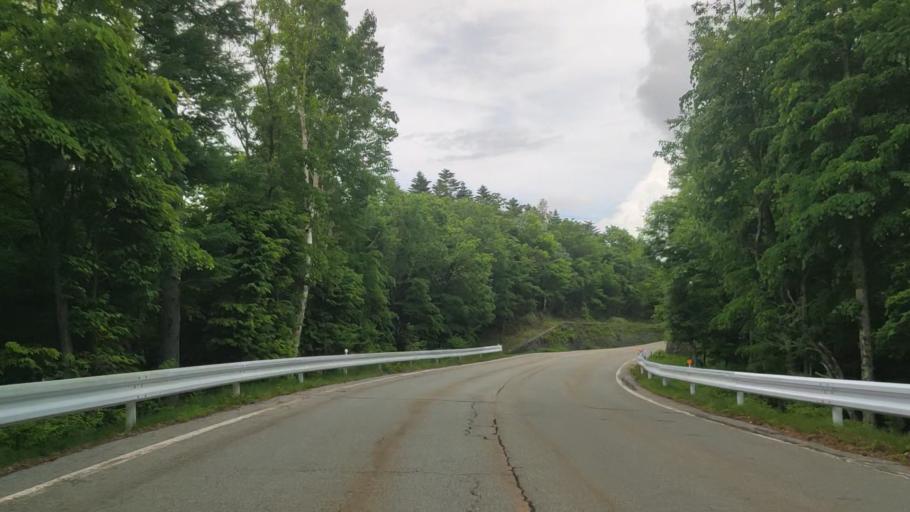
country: JP
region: Yamanashi
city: Fujikawaguchiko
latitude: 35.4141
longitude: 138.6998
